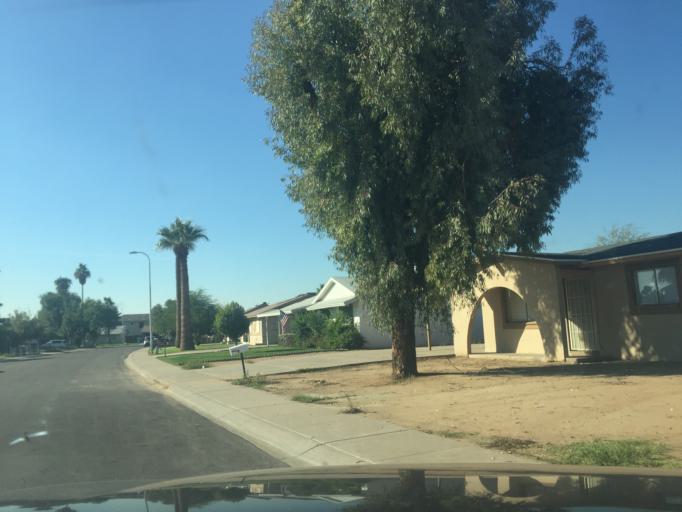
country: US
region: Arizona
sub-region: Maricopa County
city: Tolleson
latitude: 33.4774
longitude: -112.2145
